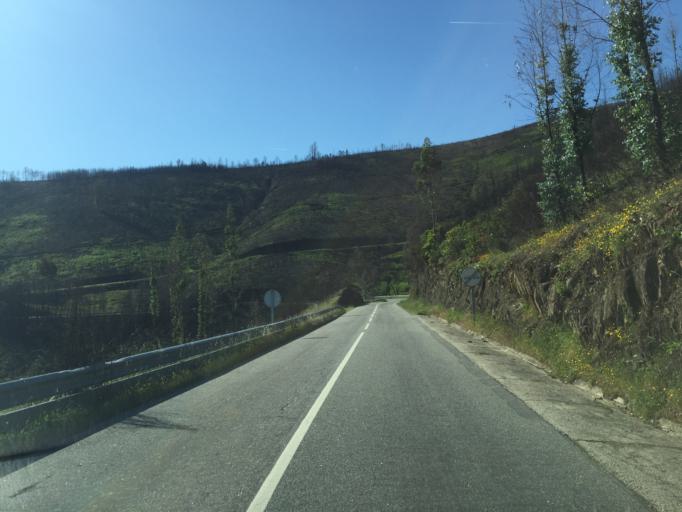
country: PT
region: Coimbra
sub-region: Pampilhosa da Serra
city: Pampilhosa da Serra
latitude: 40.0400
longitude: -7.9166
